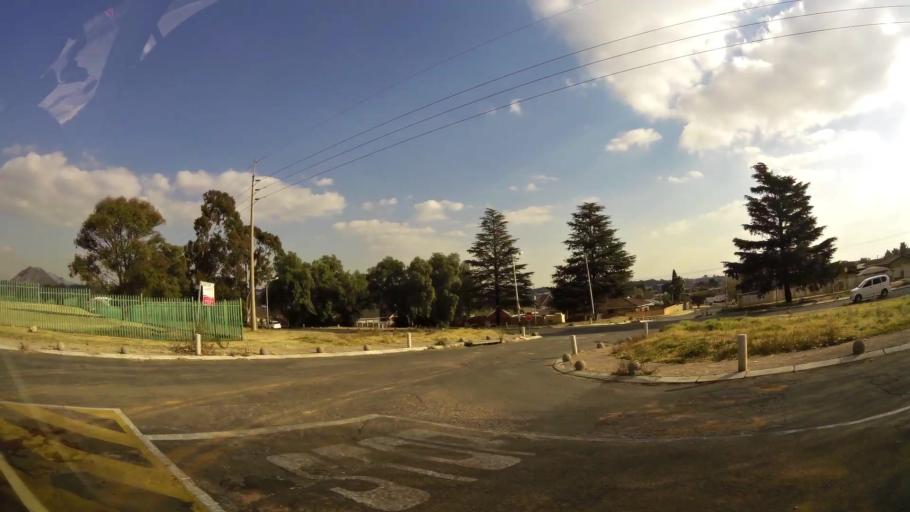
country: ZA
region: Gauteng
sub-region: West Rand District Municipality
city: Krugersdorp
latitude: -26.0906
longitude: 27.7609
